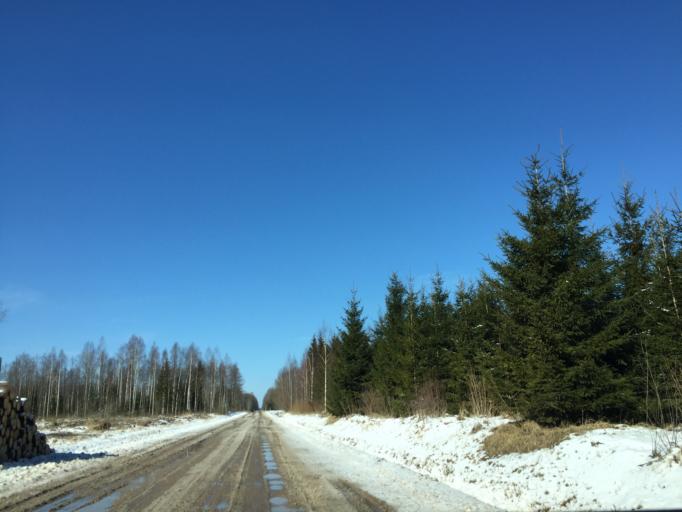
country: LV
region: Aloja
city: Staicele
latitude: 58.0272
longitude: 24.5678
